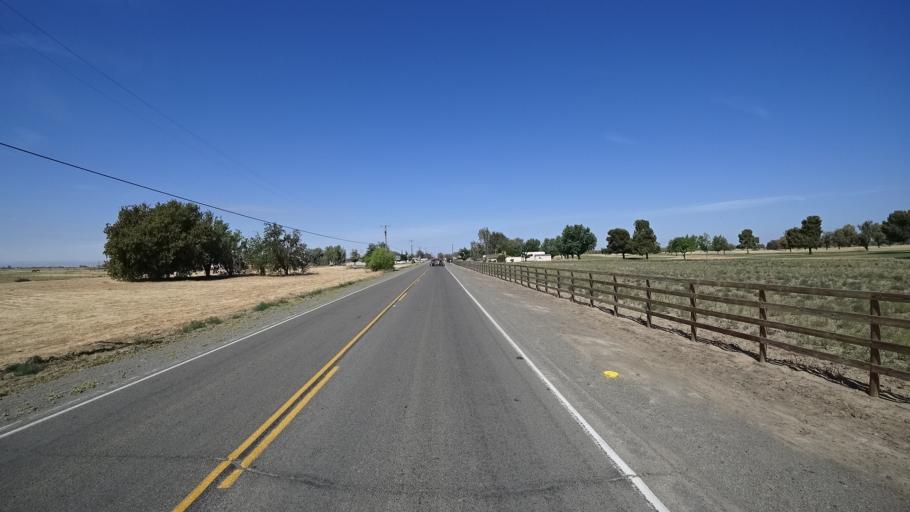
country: US
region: California
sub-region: Kings County
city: Lemoore
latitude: 36.2546
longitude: -119.7818
